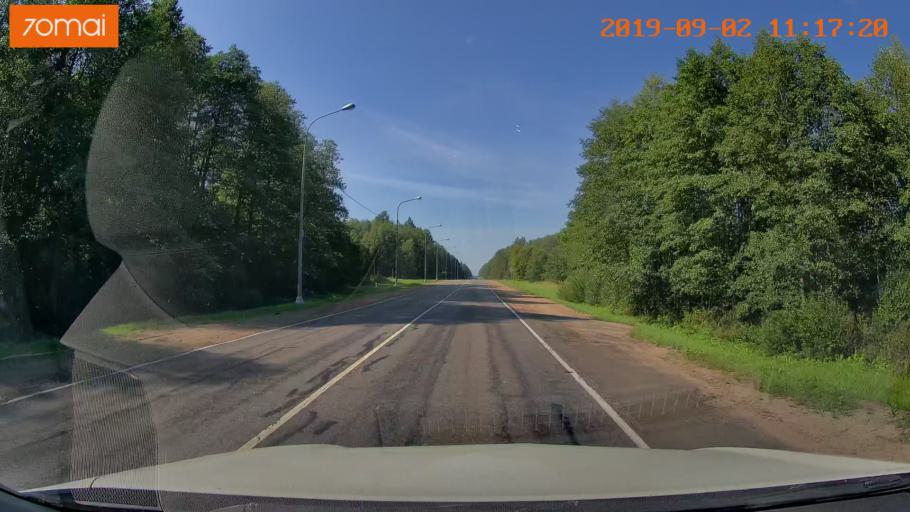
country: RU
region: Smolensk
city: Yekimovichi
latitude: 54.0625
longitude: 33.1211
